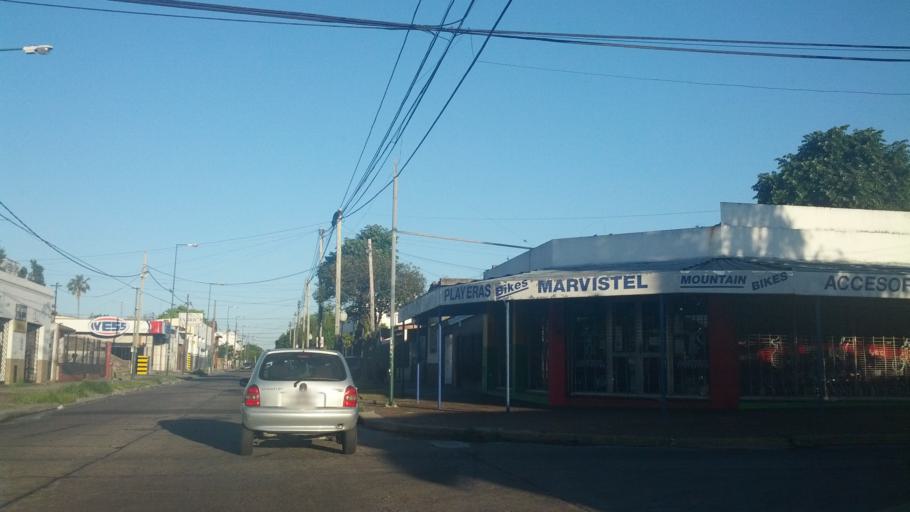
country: AR
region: Buenos Aires
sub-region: Partido de Lomas de Zamora
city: Lomas de Zamora
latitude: -34.7673
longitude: -58.4146
